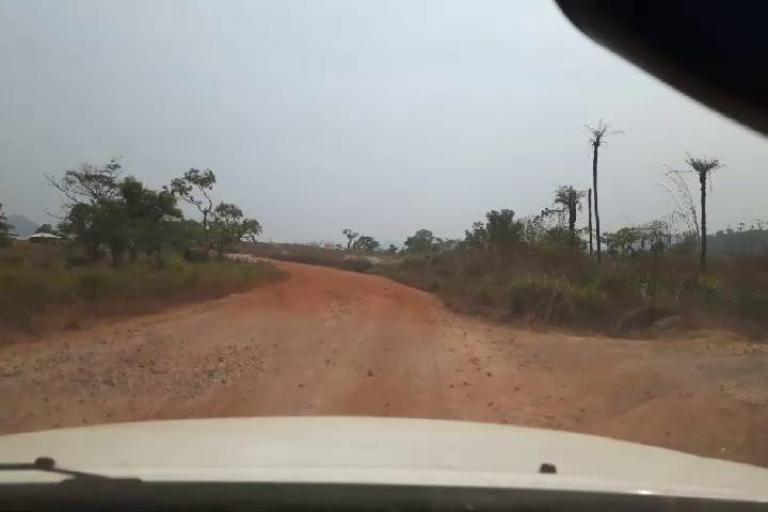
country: SL
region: Northern Province
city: Bumbuna
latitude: 9.0053
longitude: -11.7737
